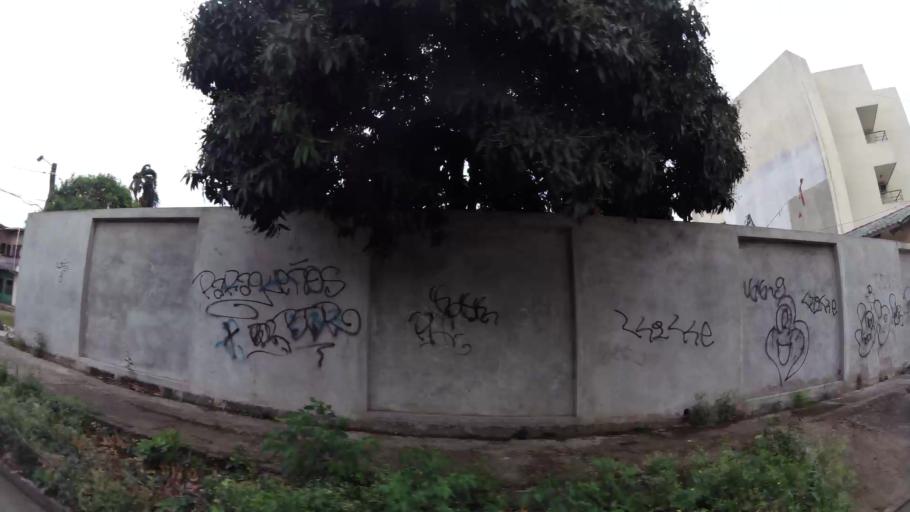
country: BO
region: Santa Cruz
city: Santa Cruz de la Sierra
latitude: -17.7713
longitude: -63.1631
